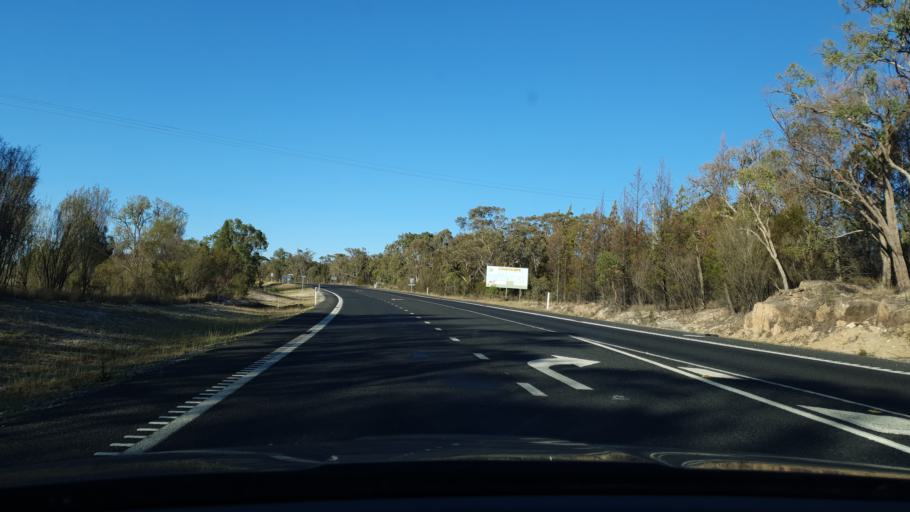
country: AU
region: Queensland
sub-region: Southern Downs
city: Stanthorpe
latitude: -28.6818
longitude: 151.9192
